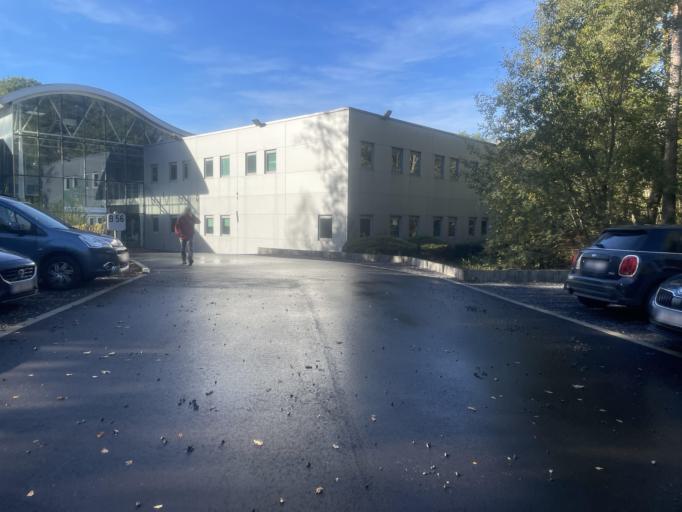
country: BE
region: Wallonia
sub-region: Province de Liege
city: Esneux
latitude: 50.5830
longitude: 5.5571
